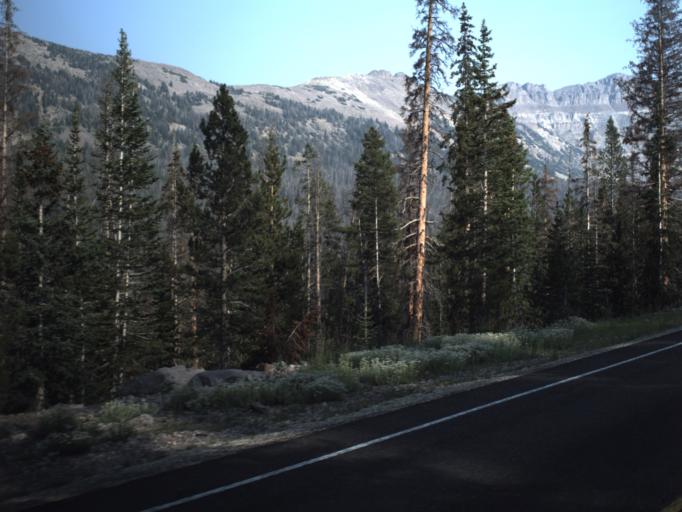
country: US
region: Utah
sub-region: Summit County
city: Kamas
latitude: 40.7554
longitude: -110.8793
